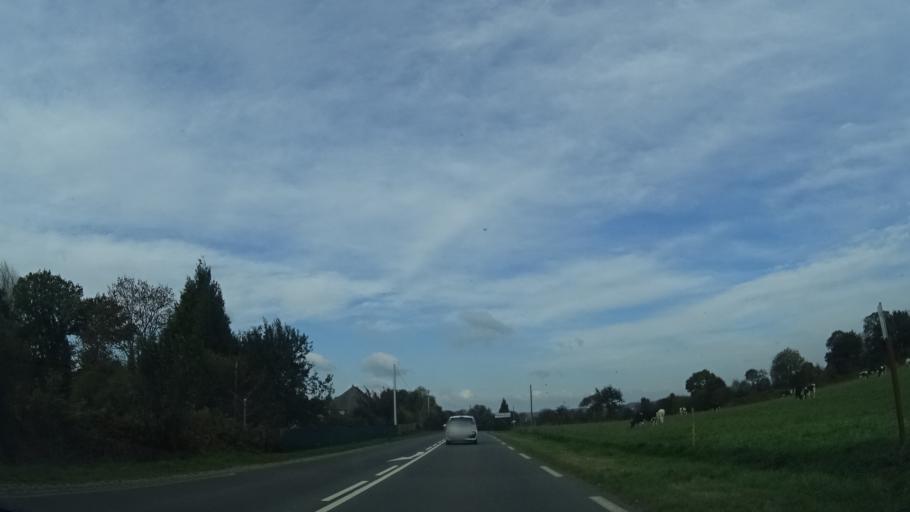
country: FR
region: Brittany
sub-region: Departement d'Ille-et-Vilaine
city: Combourg
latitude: 48.3825
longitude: -1.7538
